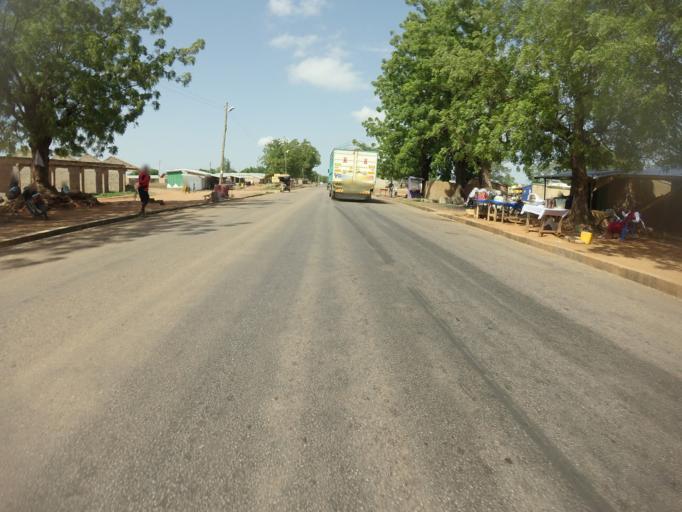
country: GH
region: Upper East
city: Bawku
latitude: 11.0692
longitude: -0.2082
